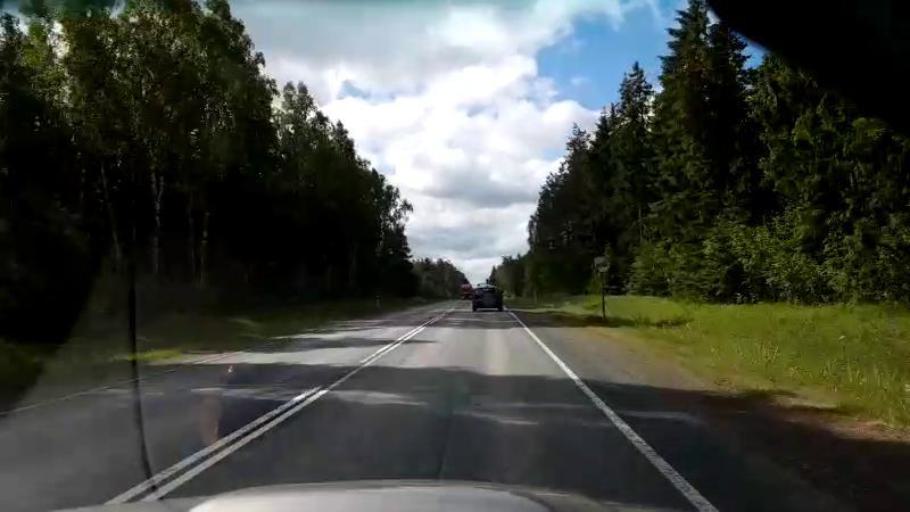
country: EE
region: Harju
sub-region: Saue linn
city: Saue
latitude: 59.2037
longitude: 24.4975
